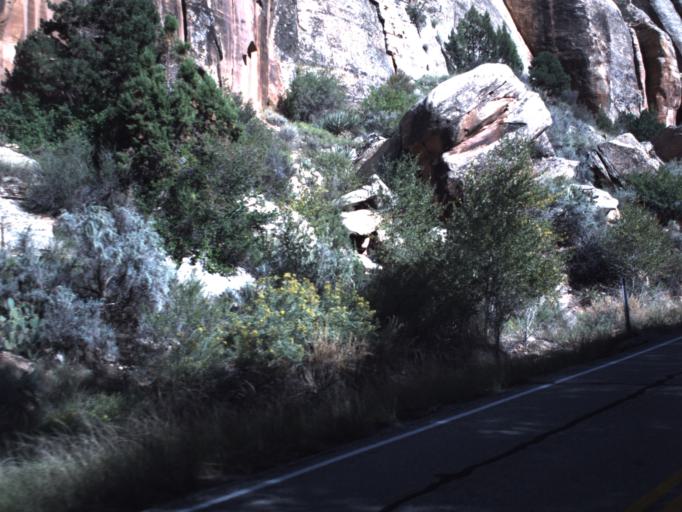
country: US
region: Utah
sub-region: San Juan County
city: Monticello
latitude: 37.9956
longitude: -109.5279
